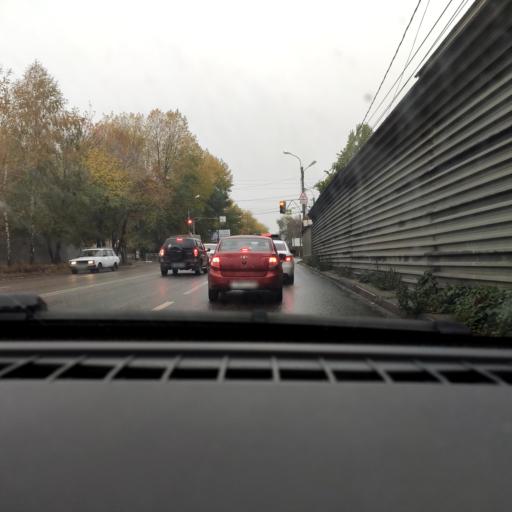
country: RU
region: Voronezj
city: Voronezh
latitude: 51.6931
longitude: 39.2151
